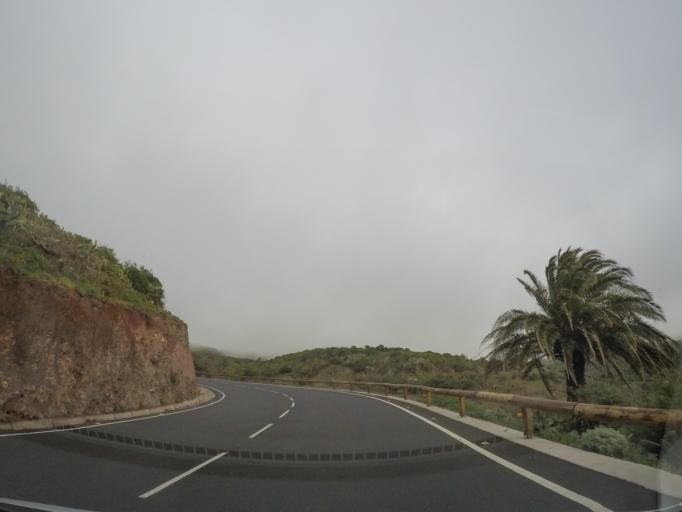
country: ES
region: Canary Islands
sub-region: Provincia de Santa Cruz de Tenerife
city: Vallehermosa
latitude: 28.1418
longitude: -17.3089
